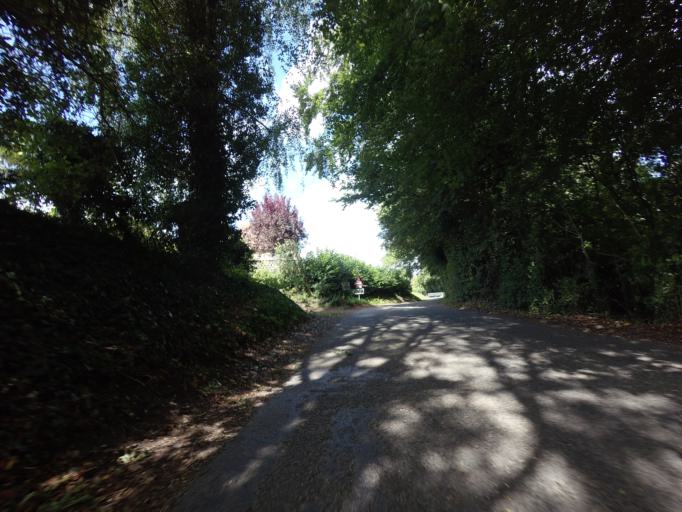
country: GB
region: England
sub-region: Kent
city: Shoreham
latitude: 51.3317
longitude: 0.1767
